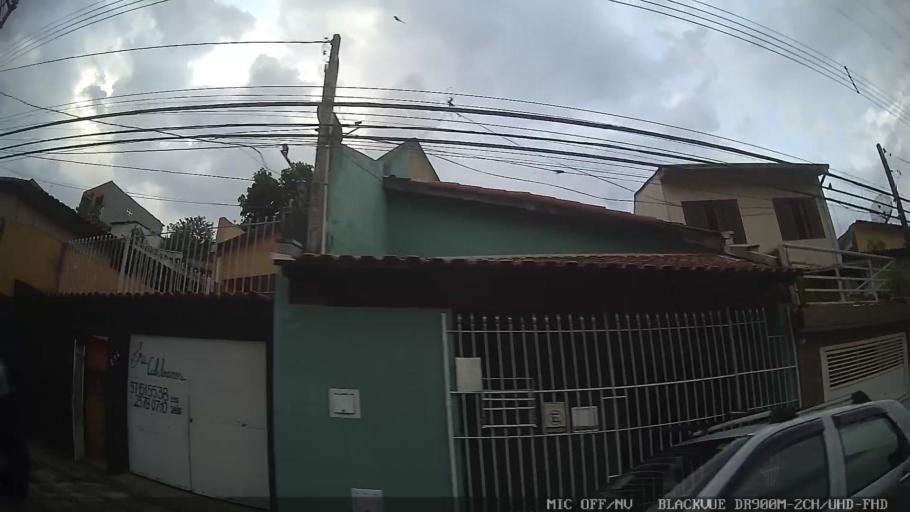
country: BR
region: Sao Paulo
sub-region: Mogi das Cruzes
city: Mogi das Cruzes
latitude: -23.5430
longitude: -46.1904
